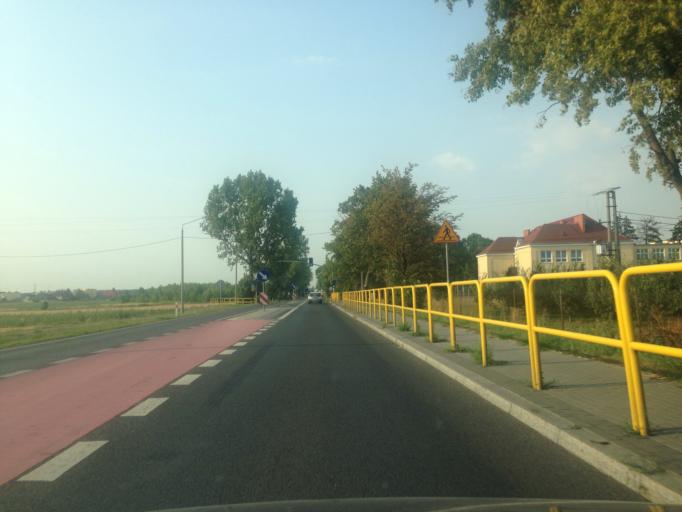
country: PL
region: Kujawsko-Pomorskie
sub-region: Powiat wloclawski
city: Fabianki
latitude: 52.7092
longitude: 19.1049
